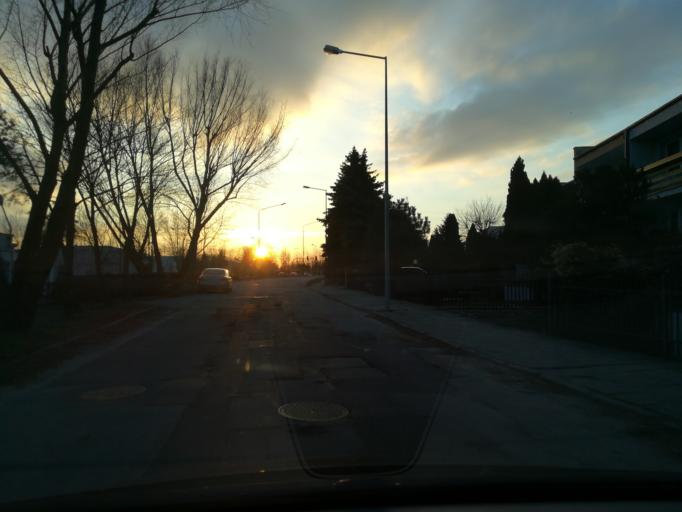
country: PL
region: Lodz Voivodeship
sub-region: Piotrkow Trybunalski
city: Piotrkow Trybunalski
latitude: 51.4065
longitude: 19.6595
